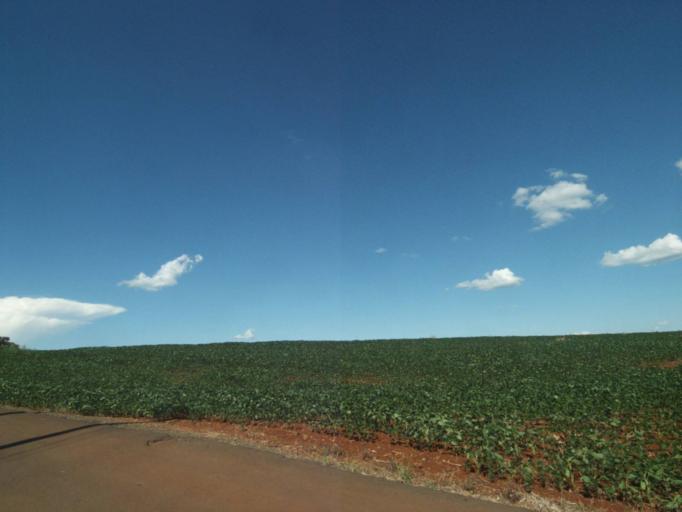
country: BR
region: Parana
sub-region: Sertanopolis
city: Sertanopolis
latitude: -23.0435
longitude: -50.8139
